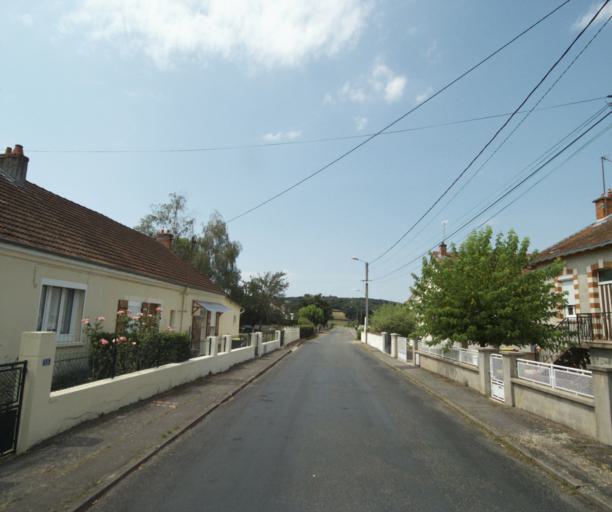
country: FR
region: Bourgogne
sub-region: Departement de Saone-et-Loire
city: Gueugnon
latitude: 46.5994
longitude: 4.0473
